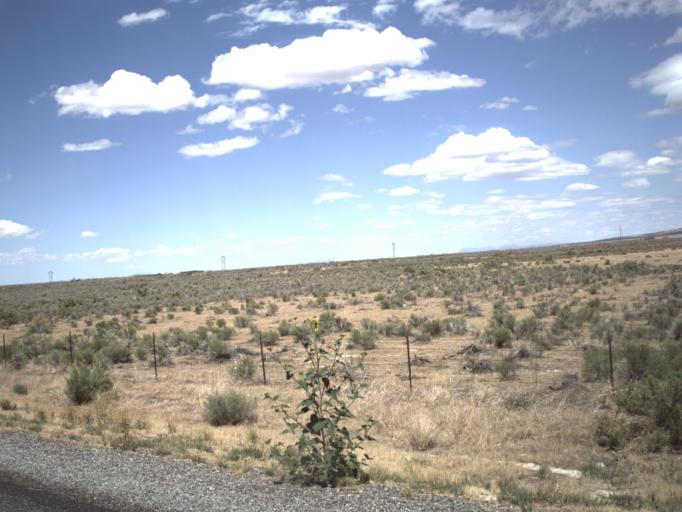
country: US
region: Utah
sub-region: Millard County
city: Fillmore
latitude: 39.1438
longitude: -112.3823
